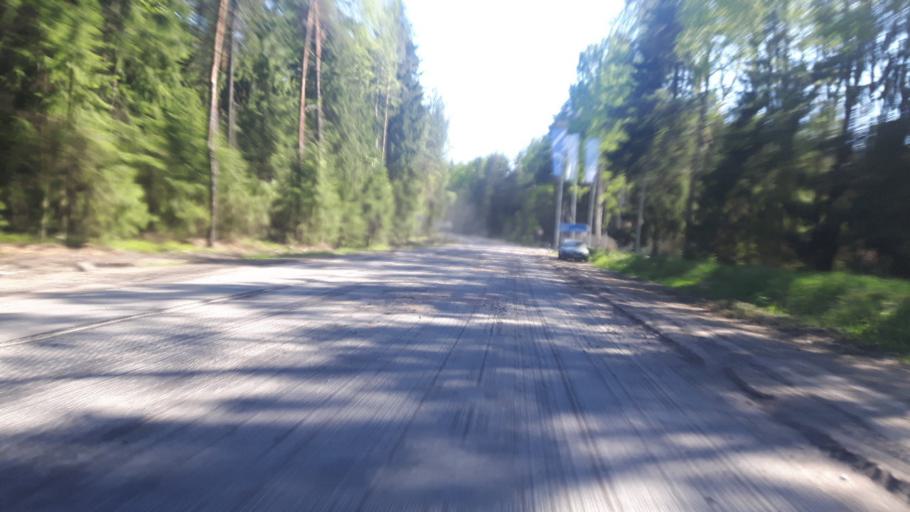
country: RU
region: Leningrad
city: Sosnovyy Bor
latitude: 60.2305
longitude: 29.0021
